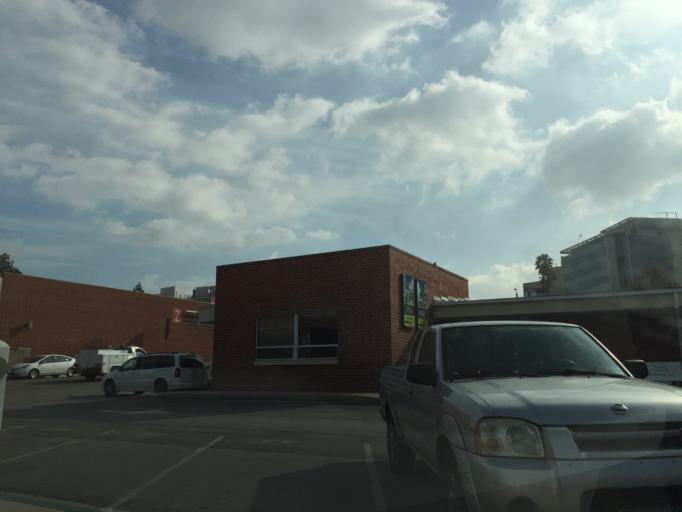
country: US
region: California
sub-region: Los Angeles County
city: Boyle Heights
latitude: 34.0642
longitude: -118.2051
